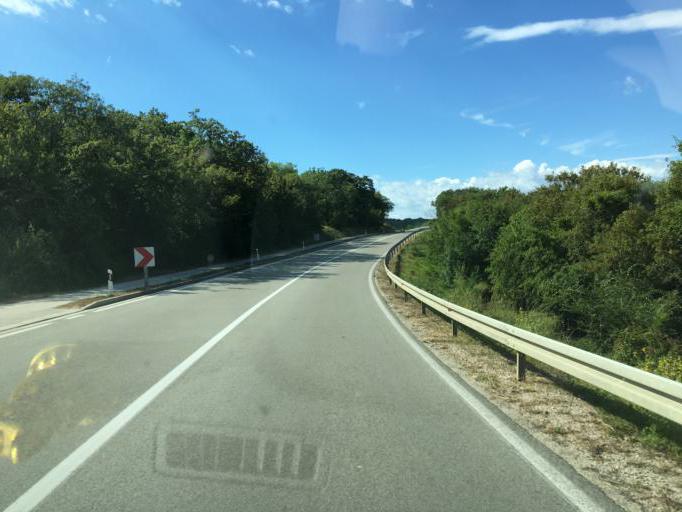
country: HR
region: Primorsko-Goranska
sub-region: Grad Krk
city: Krk
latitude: 45.0728
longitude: 14.5506
